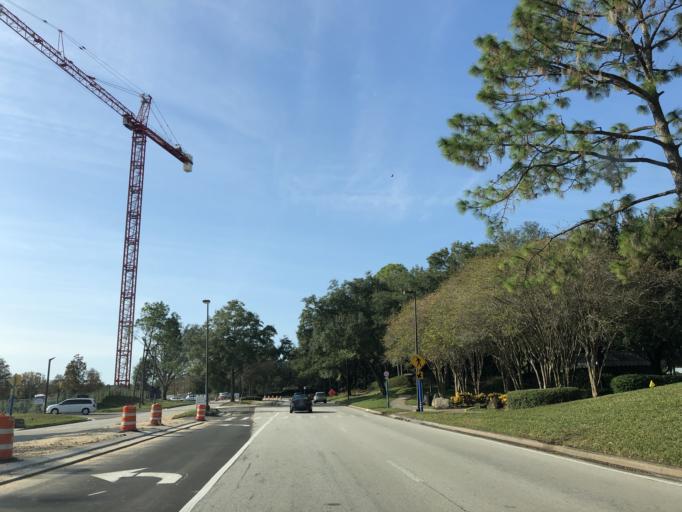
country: US
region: Florida
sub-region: Osceola County
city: Celebration
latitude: 28.3647
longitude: -81.5606
